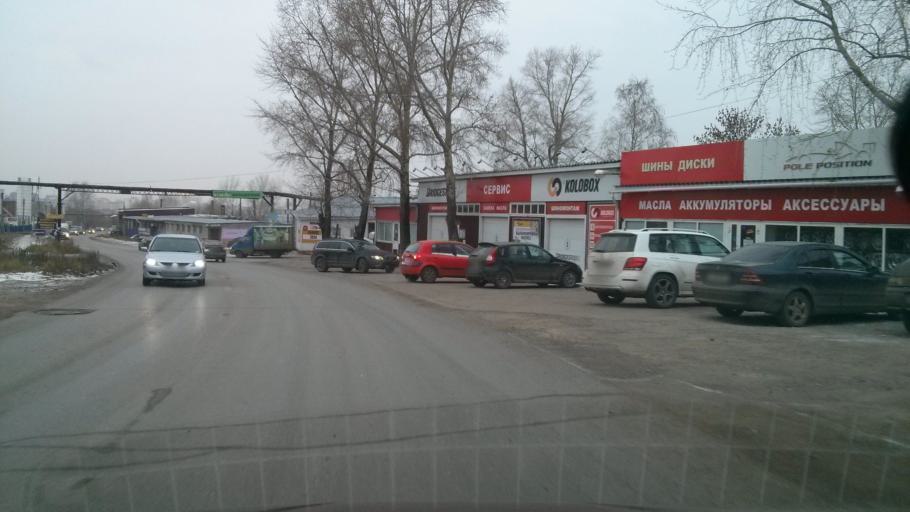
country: RU
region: Nizjnij Novgorod
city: Bor
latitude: 56.3068
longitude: 44.0609
